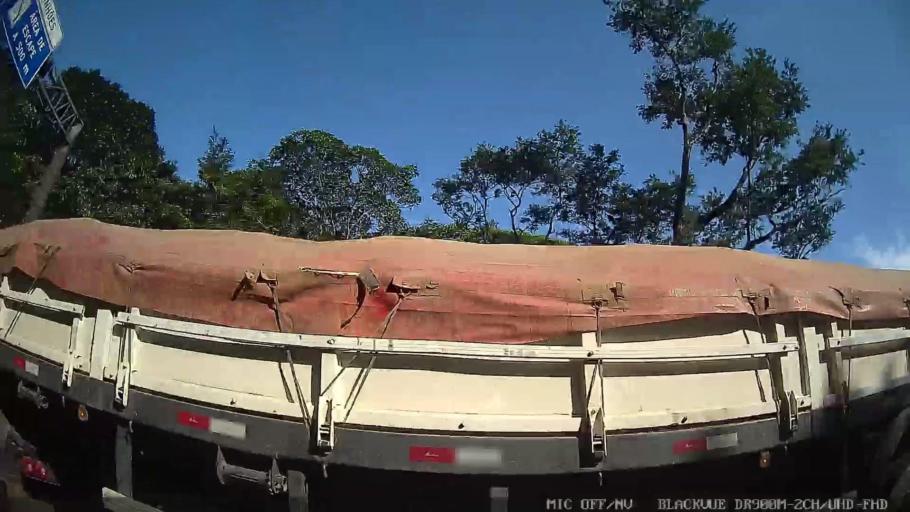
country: BR
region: Sao Paulo
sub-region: Cubatao
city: Cubatao
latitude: -23.8960
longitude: -46.4897
